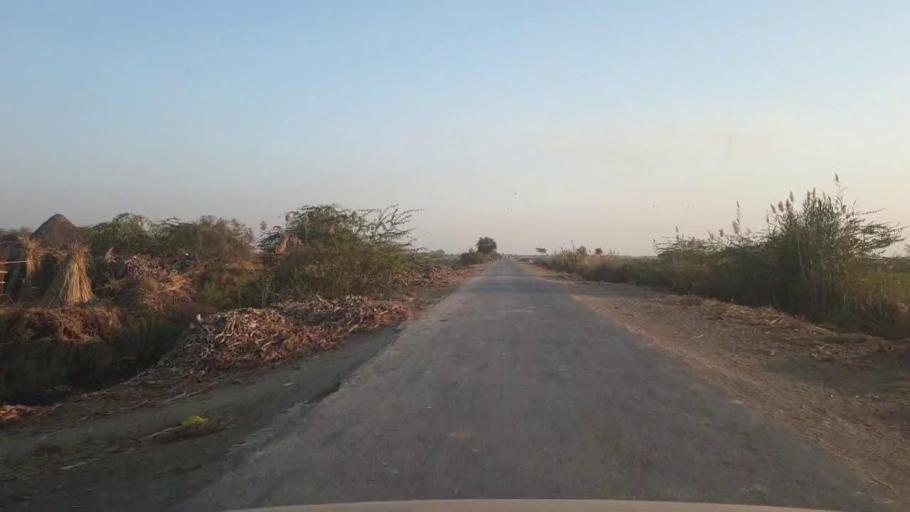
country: PK
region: Sindh
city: Chambar
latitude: 25.2912
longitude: 68.9071
